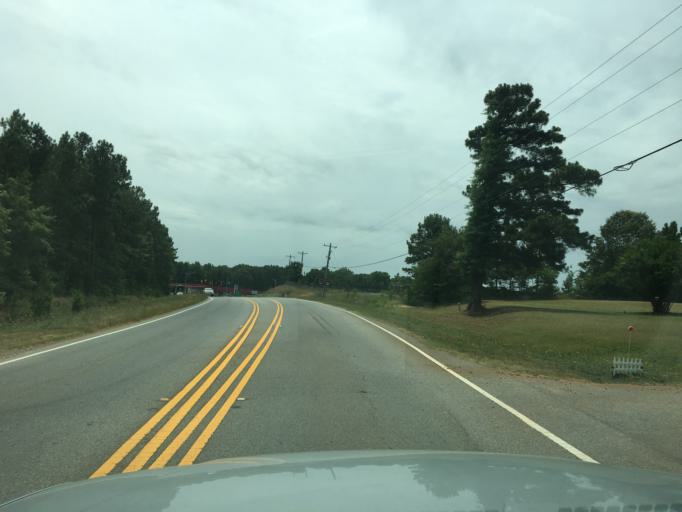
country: US
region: South Carolina
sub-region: Anderson County
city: Centerville
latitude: 34.5316
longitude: -82.8033
